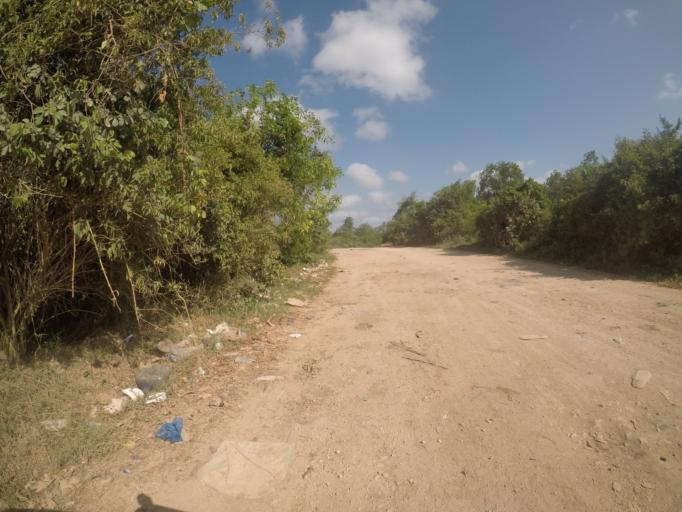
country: TZ
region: Zanzibar Central/South
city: Koani
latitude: -6.2190
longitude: 39.3268
